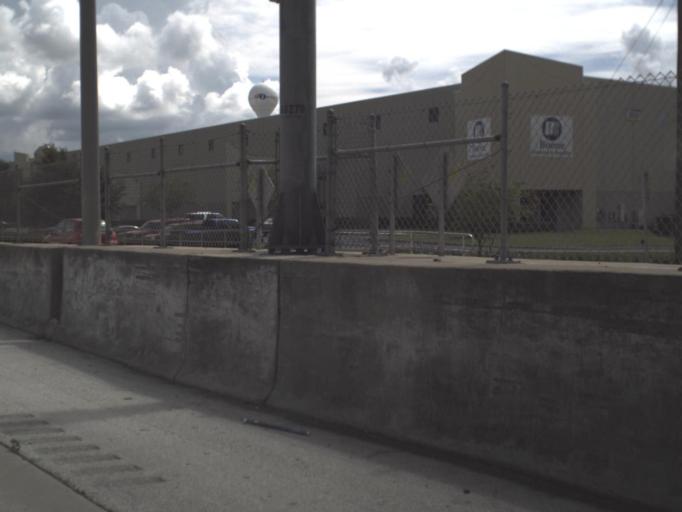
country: US
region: Florida
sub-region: Polk County
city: Winston
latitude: 28.0408
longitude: -82.0299
